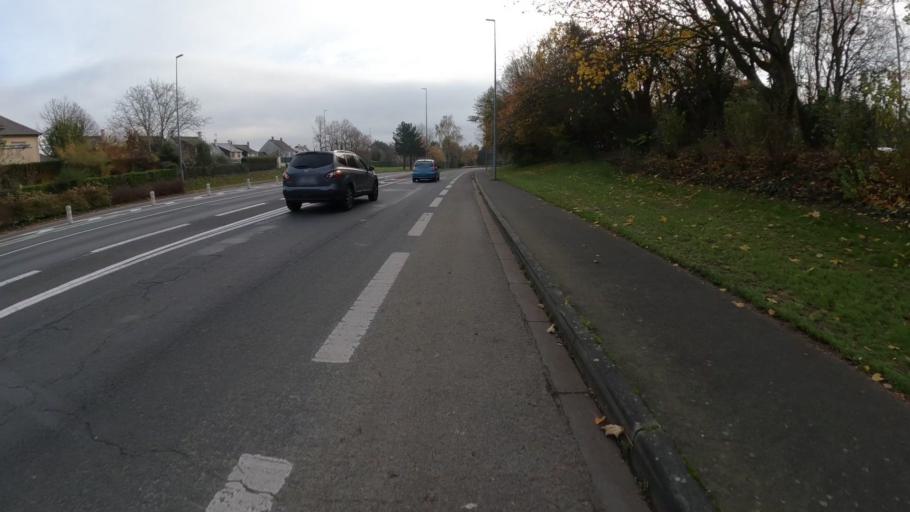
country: FR
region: Lower Normandy
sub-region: Departement du Calvados
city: Epron
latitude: 49.2045
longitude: -0.3755
